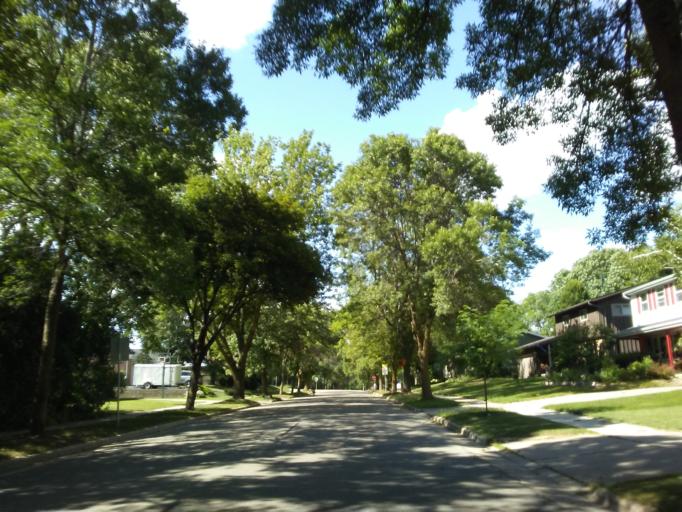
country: US
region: Wisconsin
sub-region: Dane County
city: Middleton
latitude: 43.0663
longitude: -89.4933
